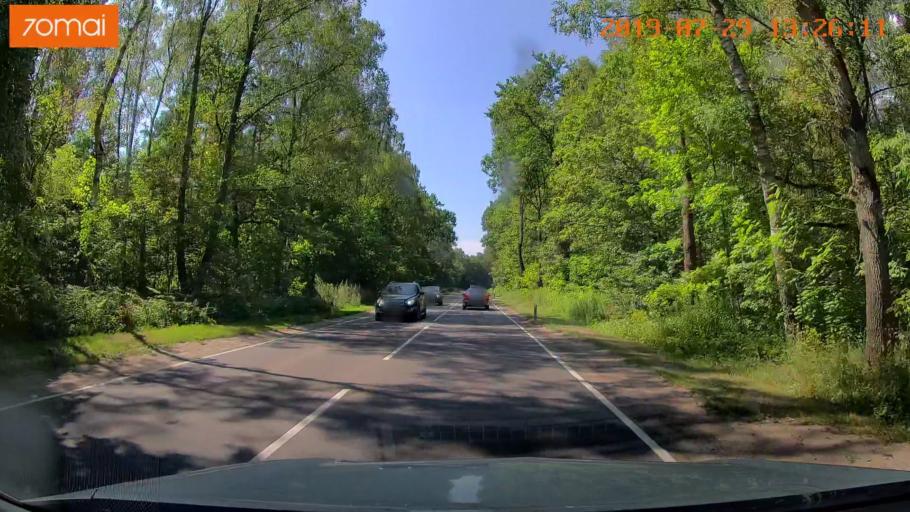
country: RU
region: Kaliningrad
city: Vzmorye
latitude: 54.7082
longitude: 20.3191
